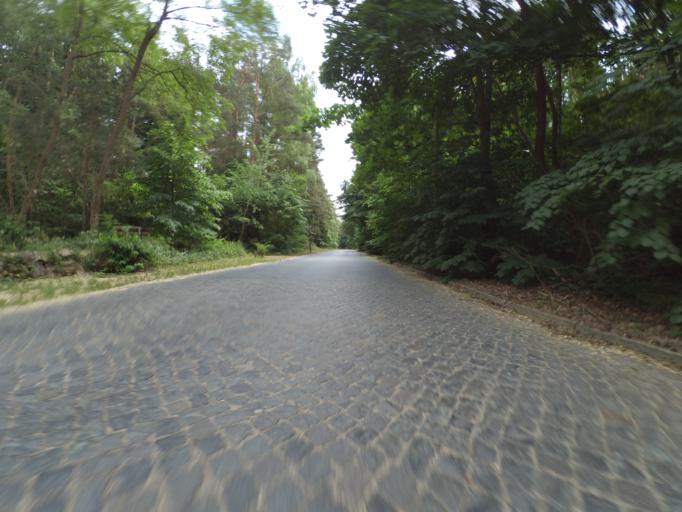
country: DE
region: Mecklenburg-Vorpommern
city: Klink
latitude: 53.5150
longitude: 12.6270
